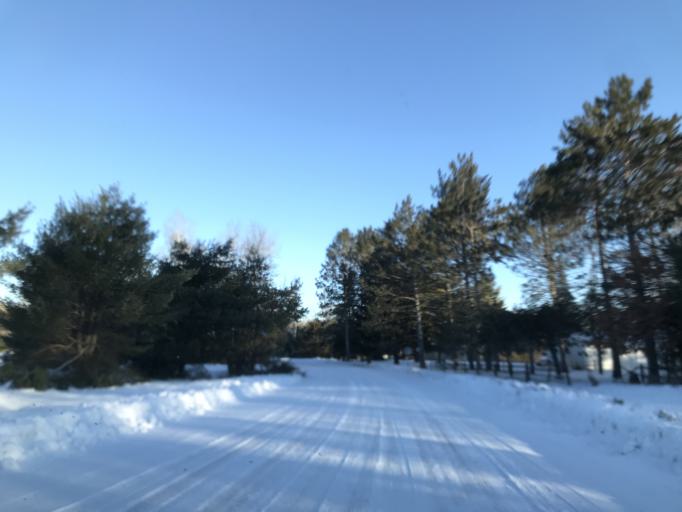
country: US
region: Michigan
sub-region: Menominee County
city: Menominee
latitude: 45.2913
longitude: -87.6954
